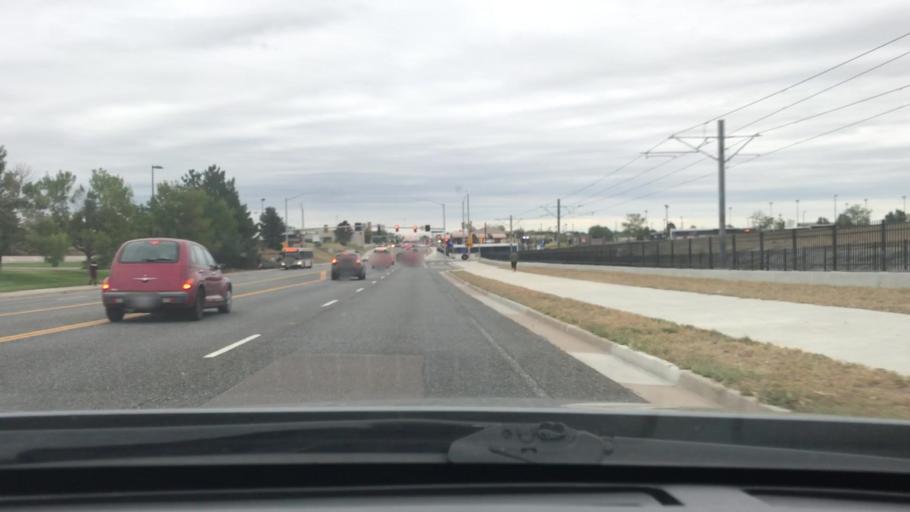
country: US
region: Colorado
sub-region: Adams County
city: Aurora
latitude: 39.7063
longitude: -104.8192
